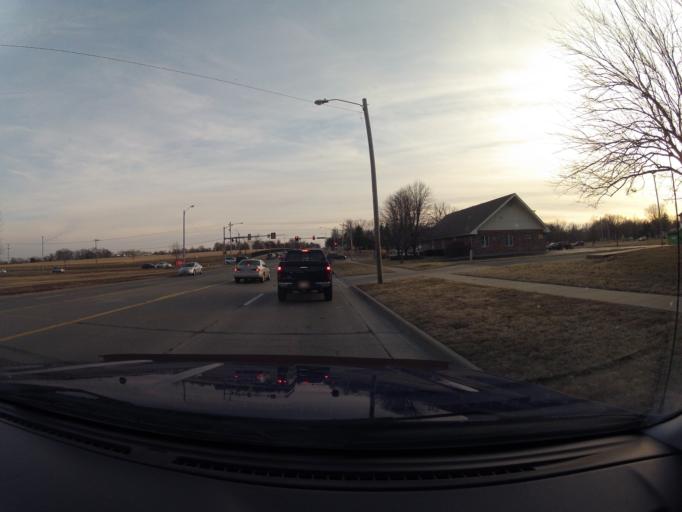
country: US
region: Kansas
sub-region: Shawnee County
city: Topeka
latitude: 39.0447
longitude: -95.7431
